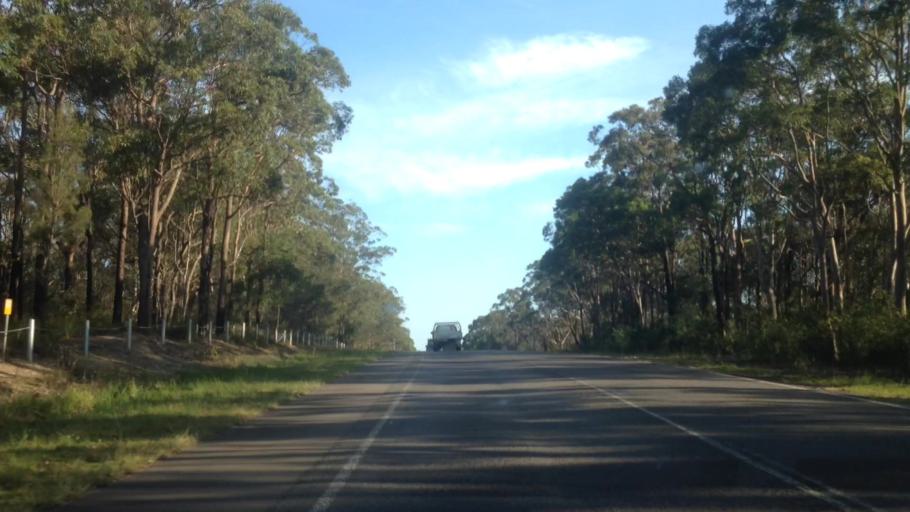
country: AU
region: New South Wales
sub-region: Lake Macquarie Shire
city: Dora Creek
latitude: -33.1425
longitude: 151.4780
